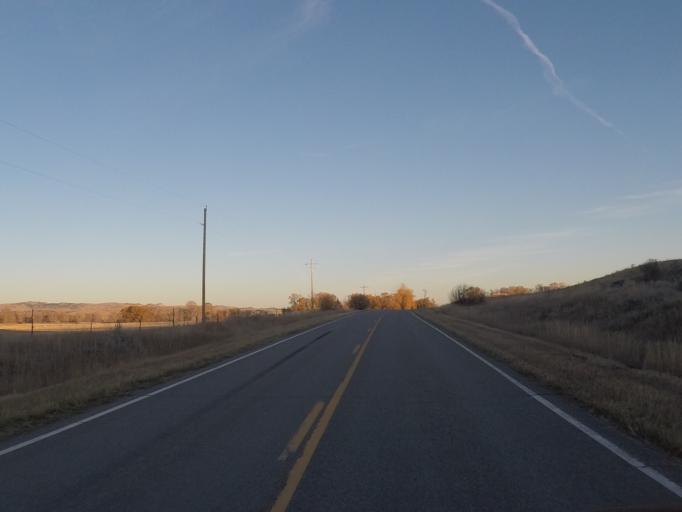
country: US
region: Montana
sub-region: Sweet Grass County
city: Big Timber
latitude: 45.7785
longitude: -109.8130
